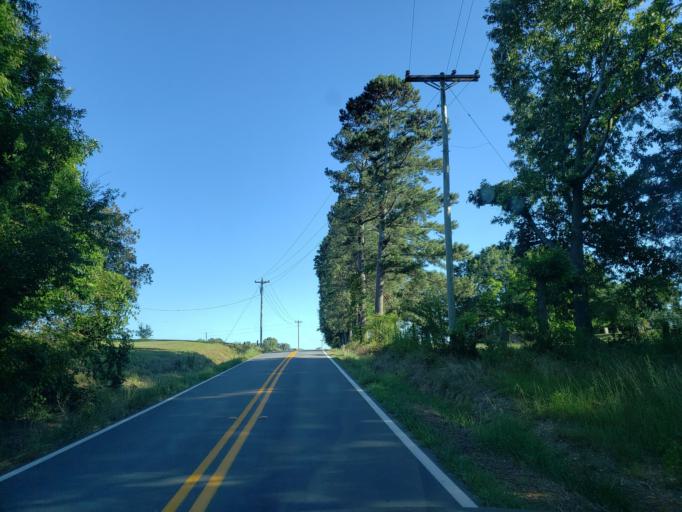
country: US
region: Georgia
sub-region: Floyd County
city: Shannon
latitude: 34.4857
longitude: -85.1168
